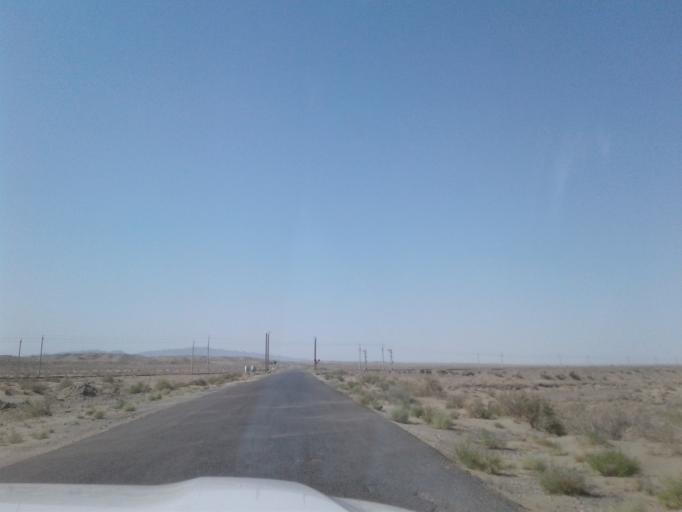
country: TM
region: Balkan
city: Gazanjyk
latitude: 39.2548
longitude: 55.3090
